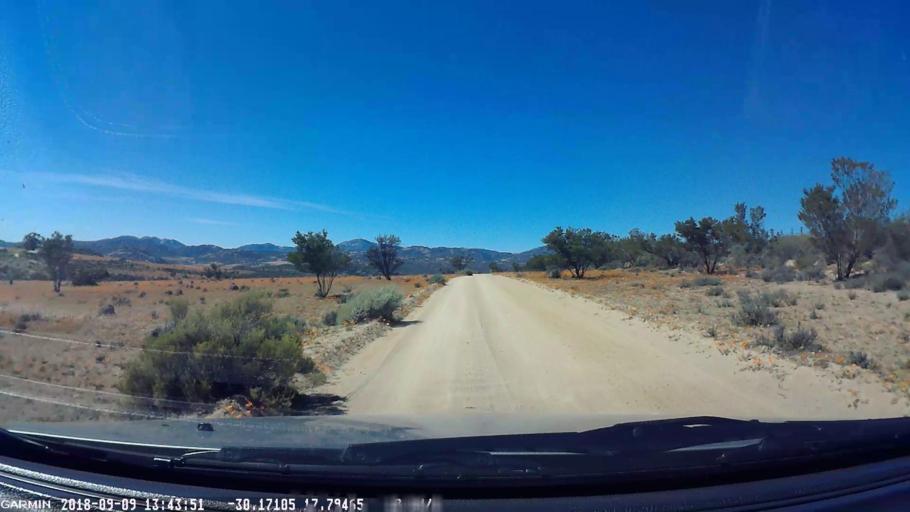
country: ZA
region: Northern Cape
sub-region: Namakwa District Municipality
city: Garies
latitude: -30.1707
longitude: 17.7960
